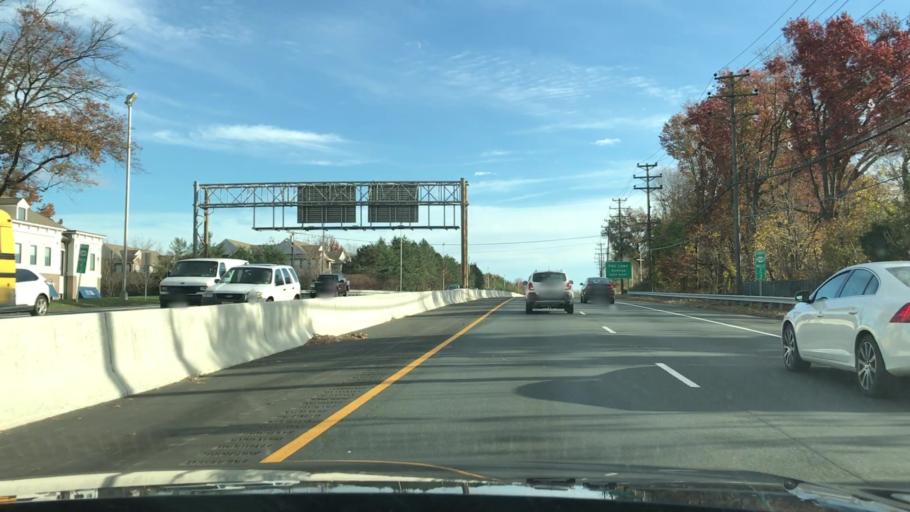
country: US
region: New Jersey
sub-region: Bergen County
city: Fair Lawn
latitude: 40.9428
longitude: -74.1298
